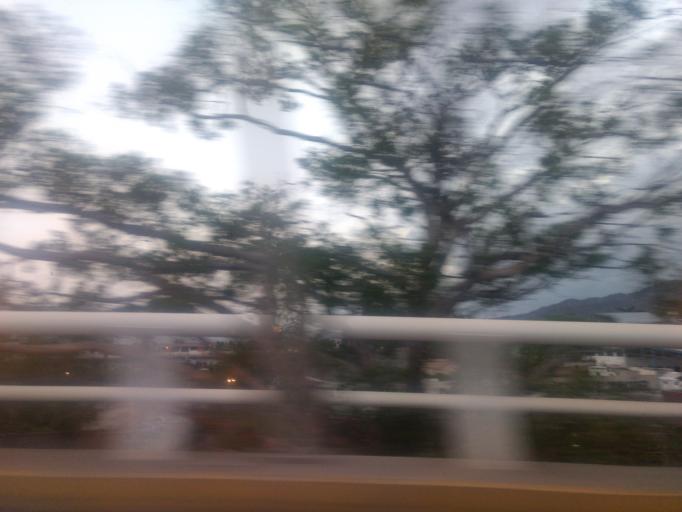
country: MX
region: Colima
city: Tapeixtles
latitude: 19.0876
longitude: -104.2951
